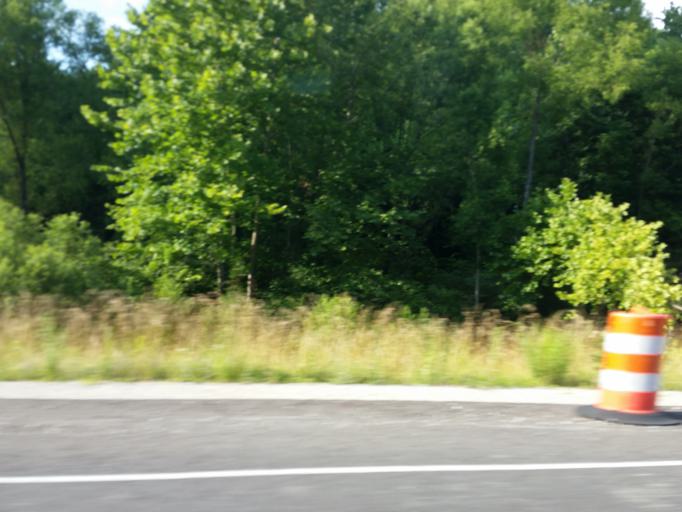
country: US
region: Tennessee
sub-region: Maury County
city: Mount Pleasant
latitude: 35.5639
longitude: -87.3629
